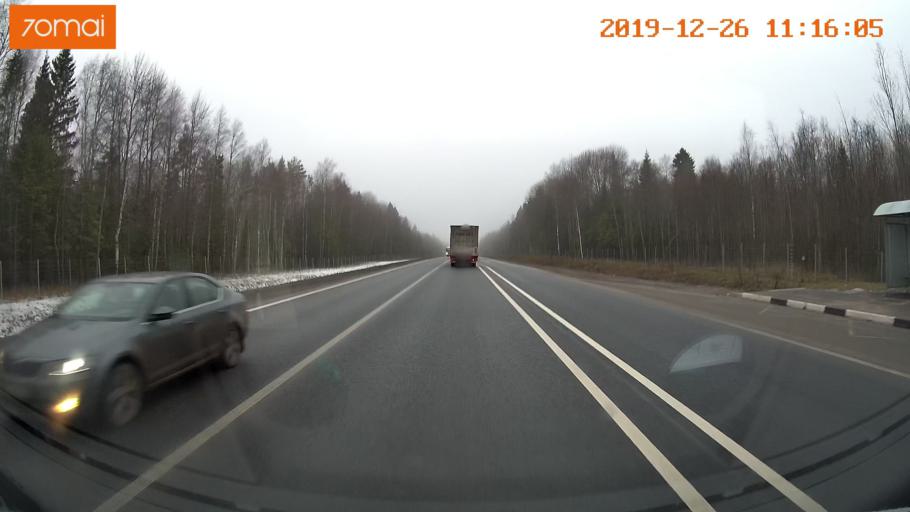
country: RU
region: Vologda
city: Chebsara
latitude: 59.1203
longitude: 39.0880
